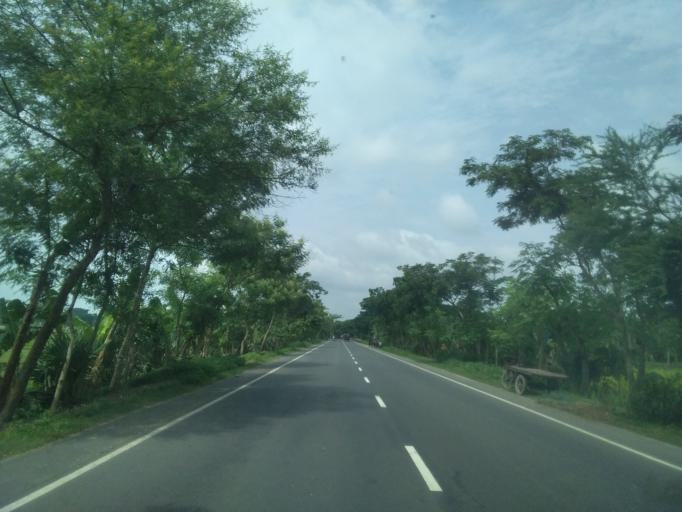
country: BD
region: Khulna
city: Kesabpur
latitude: 22.8023
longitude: 89.2331
